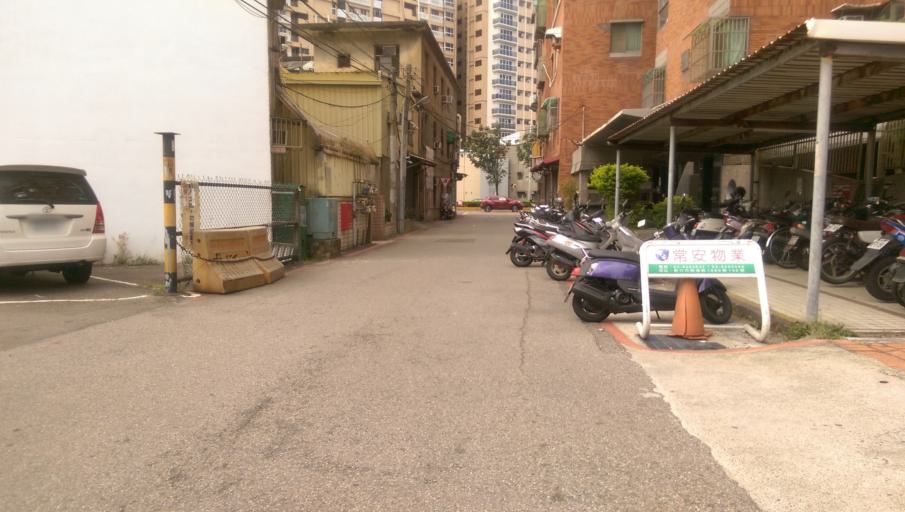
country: TW
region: Taiwan
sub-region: Hsinchu
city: Hsinchu
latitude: 24.7984
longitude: 120.9539
